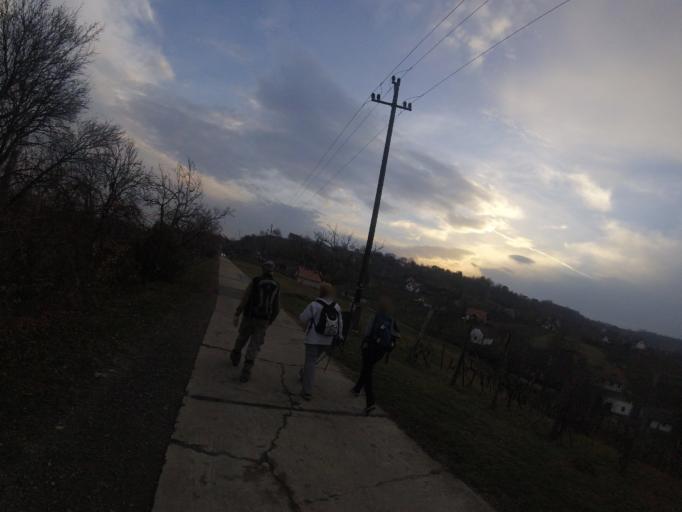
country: HU
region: Tolna
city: Szekszard
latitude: 46.3434
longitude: 18.6934
